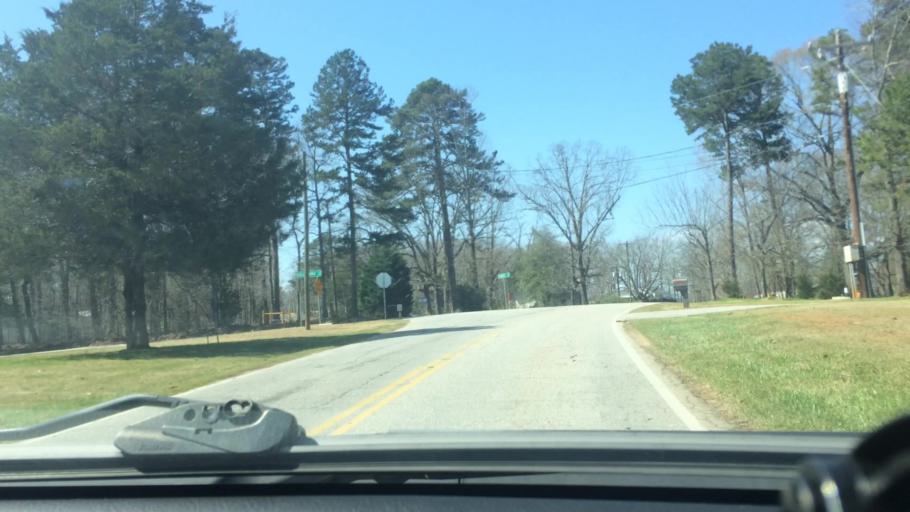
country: US
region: South Carolina
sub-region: Anderson County
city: Powdersville
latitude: 34.7903
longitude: -82.5029
